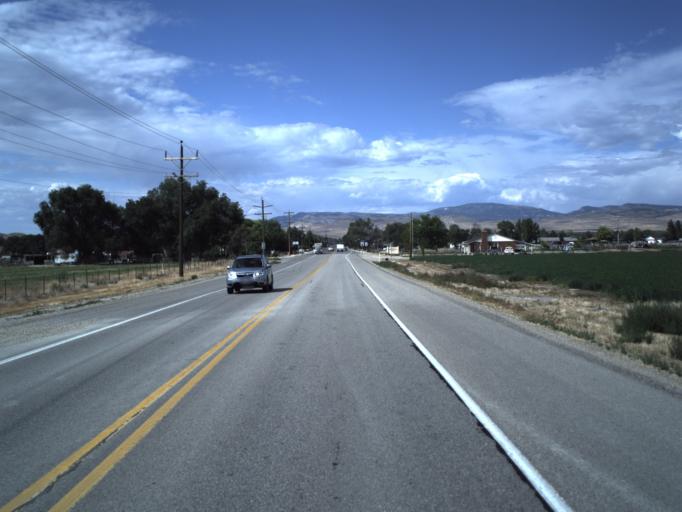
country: US
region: Utah
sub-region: Sanpete County
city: Centerfield
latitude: 39.1151
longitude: -111.8195
